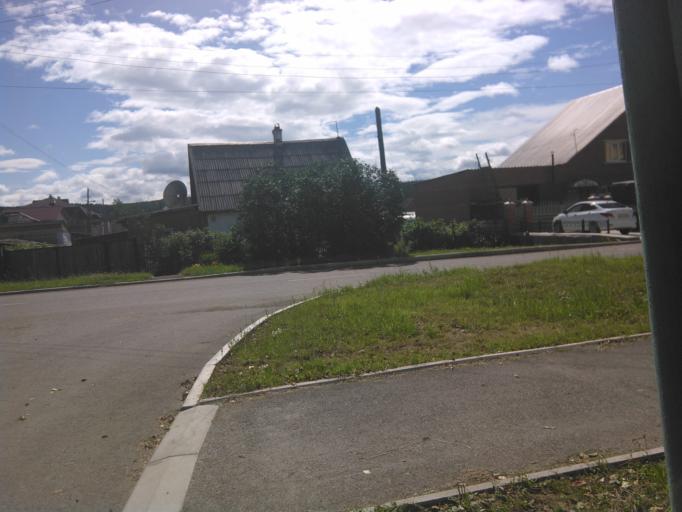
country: RU
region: Sverdlovsk
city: Krasnotur'insk
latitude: 59.7592
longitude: 60.1894
